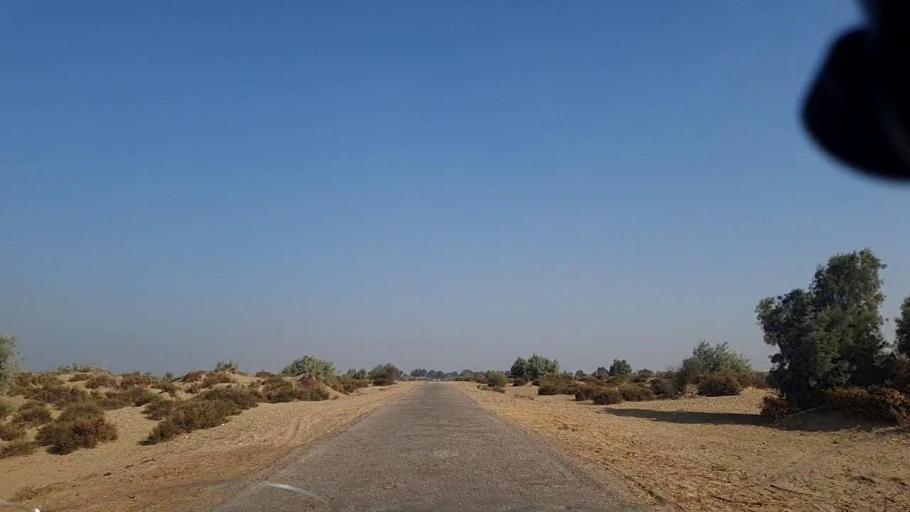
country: PK
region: Sindh
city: Khanpur
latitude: 27.6867
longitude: 69.4742
